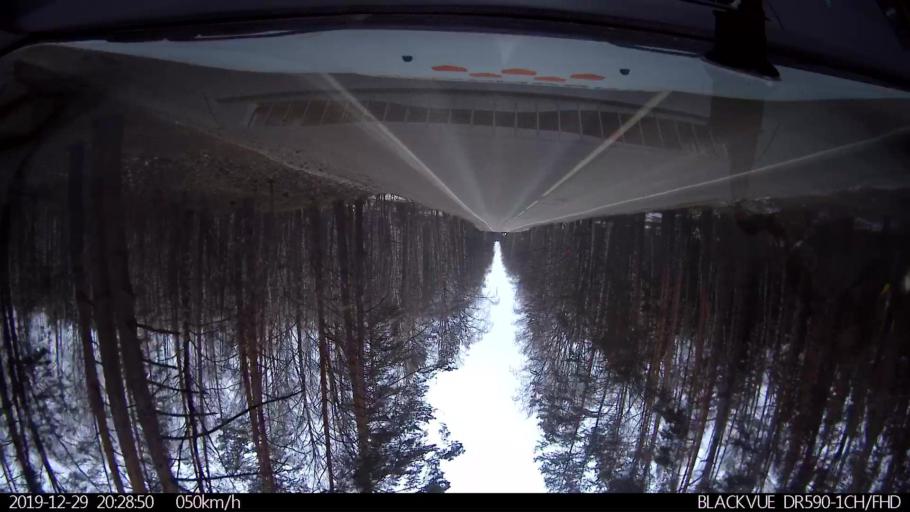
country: RU
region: Nizjnij Novgorod
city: Afonino
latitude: 56.1845
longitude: 44.1096
